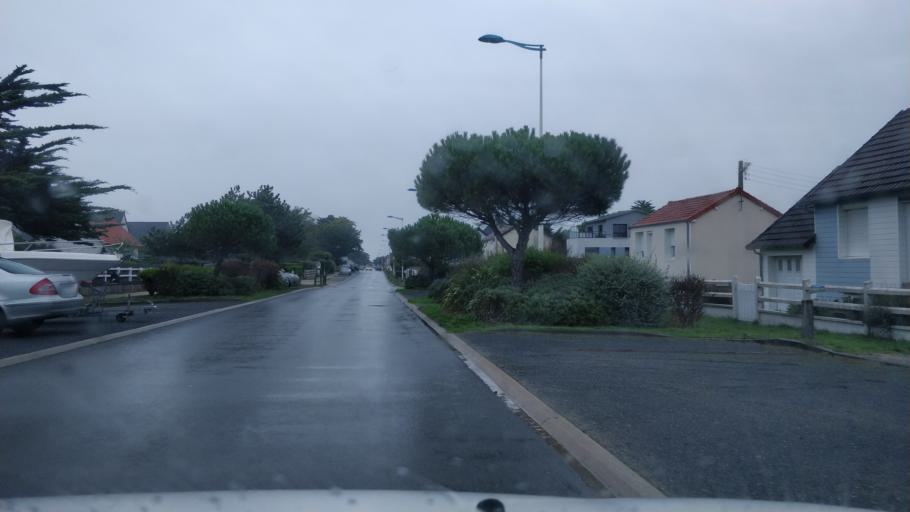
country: FR
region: Lower Normandy
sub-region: Departement de la Manche
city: Donville-les-Bains
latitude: 48.8890
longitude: -1.5705
